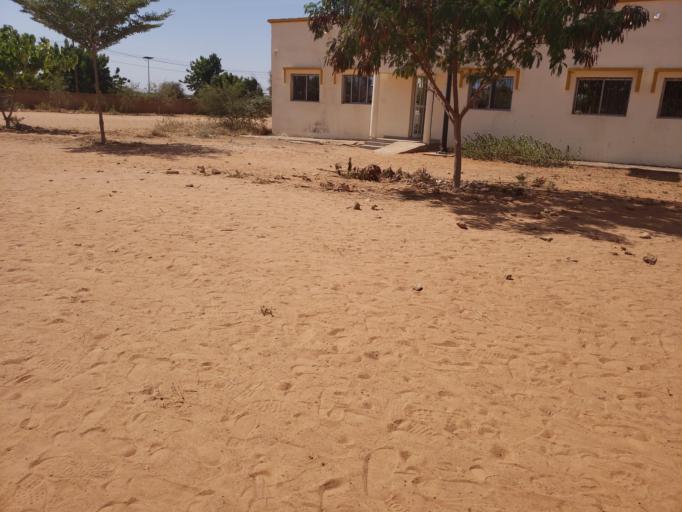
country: SN
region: Louga
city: Ndibene Dahra
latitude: 15.3994
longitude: -15.1325
